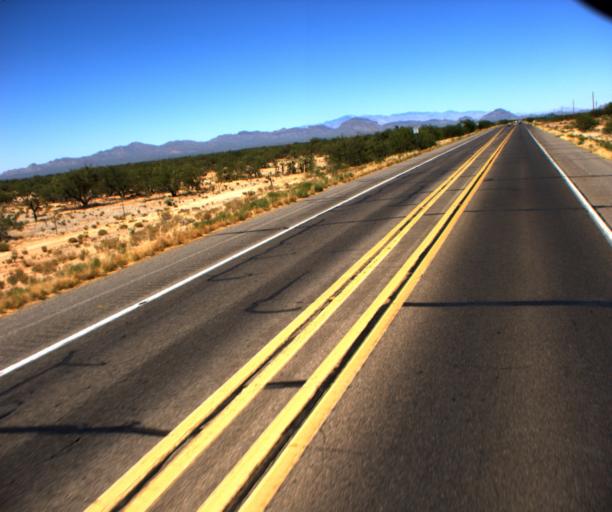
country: US
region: Arizona
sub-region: Pima County
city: Three Points
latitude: 32.0944
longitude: -111.2689
